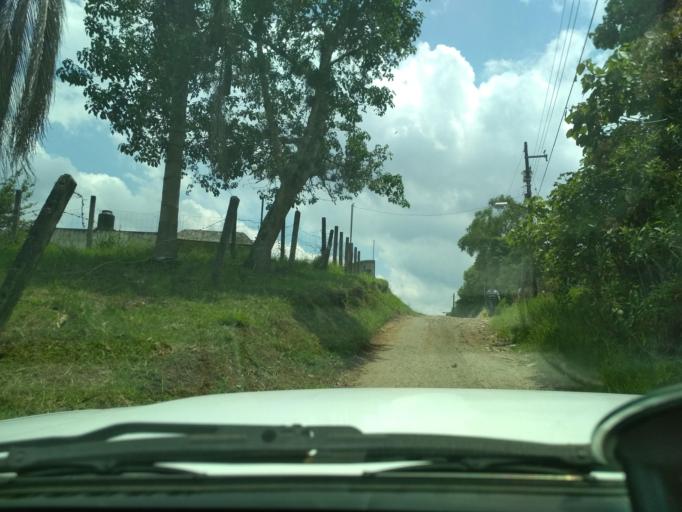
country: MX
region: Veracruz
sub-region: Cordoba
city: San Jose de Abajo [Unidad Habitacional]
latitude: 18.9193
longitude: -96.9564
